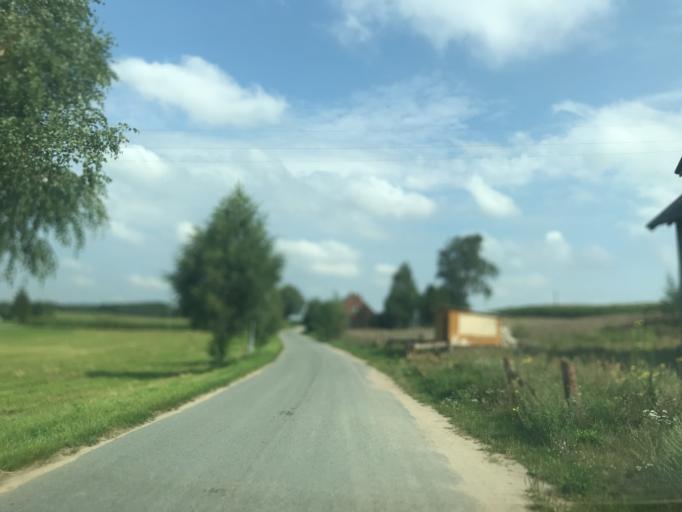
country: PL
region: Warmian-Masurian Voivodeship
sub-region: Powiat nowomiejski
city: Kurzetnik
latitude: 53.4021
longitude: 19.4548
